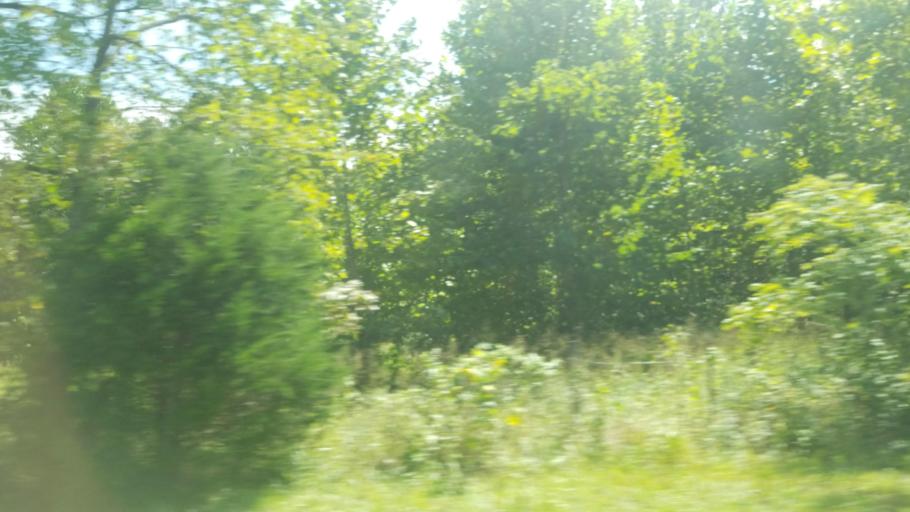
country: US
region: Illinois
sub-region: Williamson County
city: Johnston City
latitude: 37.7843
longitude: -88.8156
